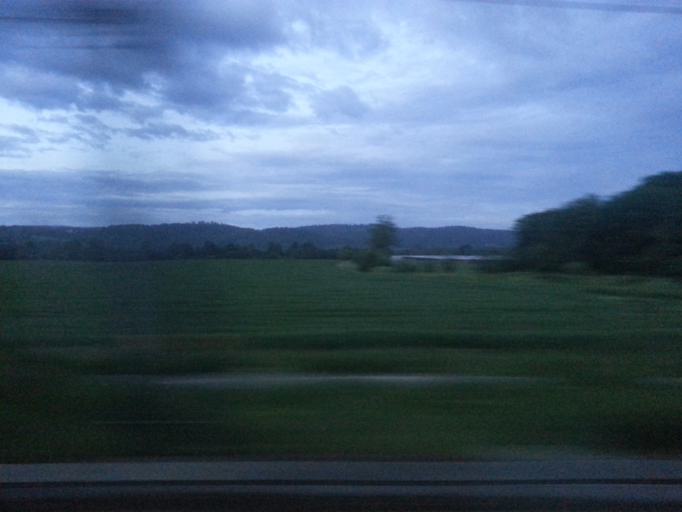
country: NO
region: Akershus
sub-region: Skedsmo
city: Lillestrom
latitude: 59.9746
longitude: 11.0702
